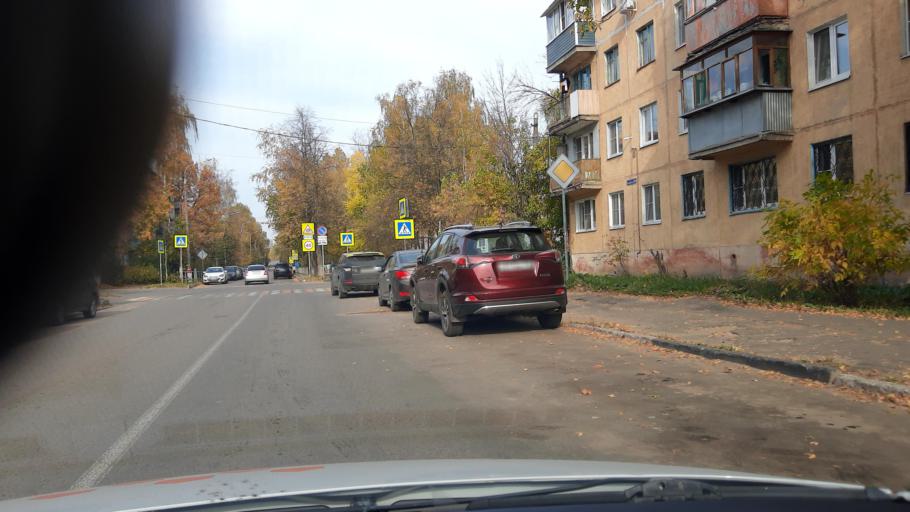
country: RU
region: Moskovskaya
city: Elektrostal'
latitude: 55.7997
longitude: 38.4346
